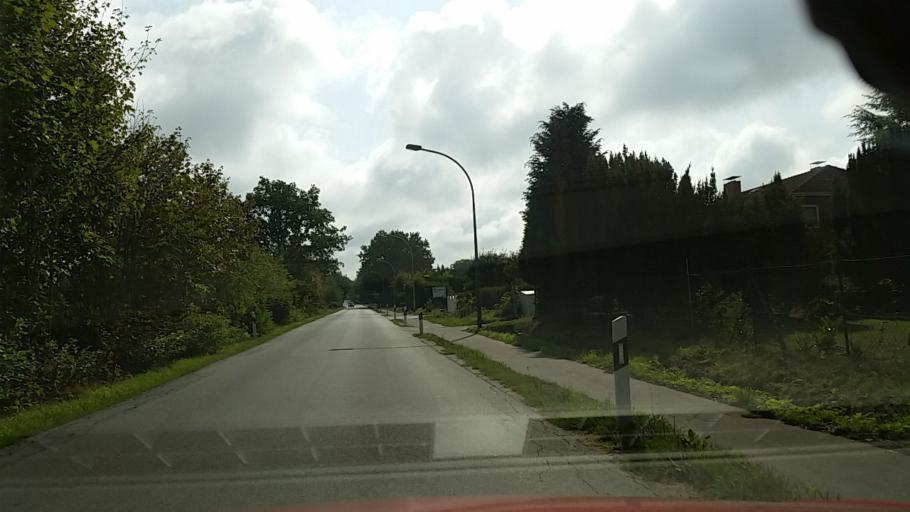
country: DE
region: Schleswig-Holstein
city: Pinneberg
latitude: 53.6313
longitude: 9.7717
